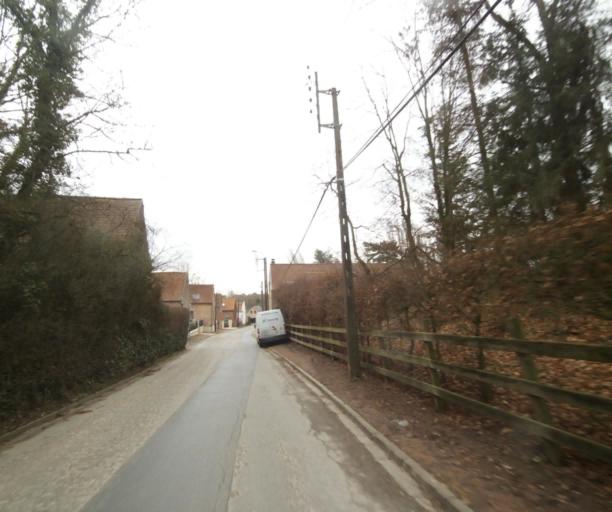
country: FR
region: Nord-Pas-de-Calais
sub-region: Departement du Nord
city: Sebourg
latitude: 50.3513
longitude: 3.6452
